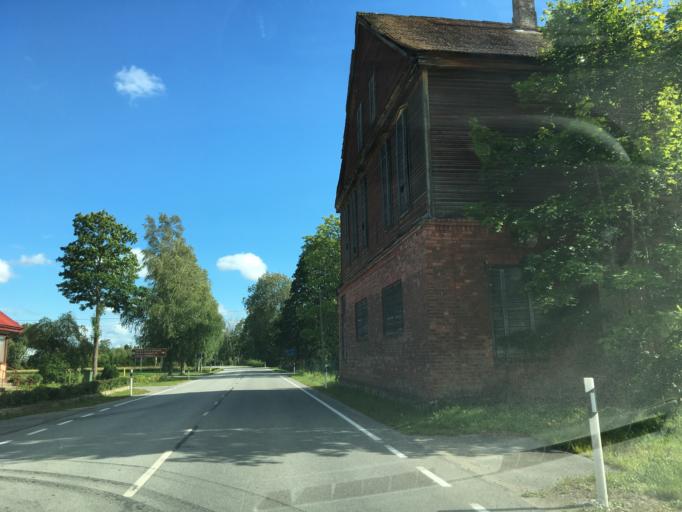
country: EE
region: Paernumaa
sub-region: Vaendra vald (alev)
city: Vandra
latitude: 58.6568
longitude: 25.0507
